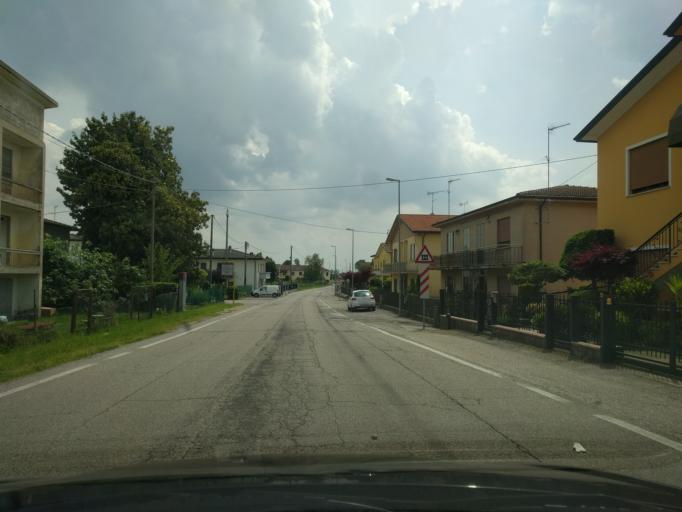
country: IT
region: Veneto
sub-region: Provincia di Rovigo
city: Lendinara
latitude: 45.0785
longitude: 11.5587
